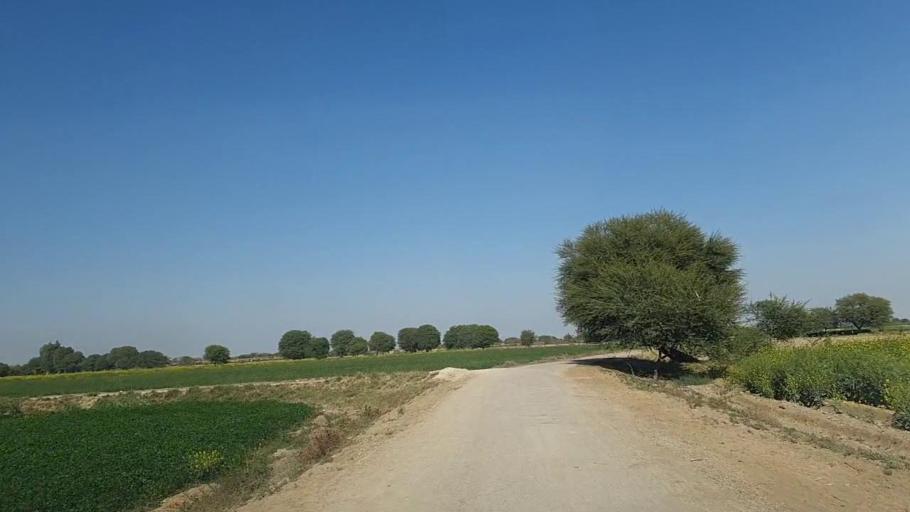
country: PK
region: Sindh
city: Naukot
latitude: 25.0111
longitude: 69.3572
